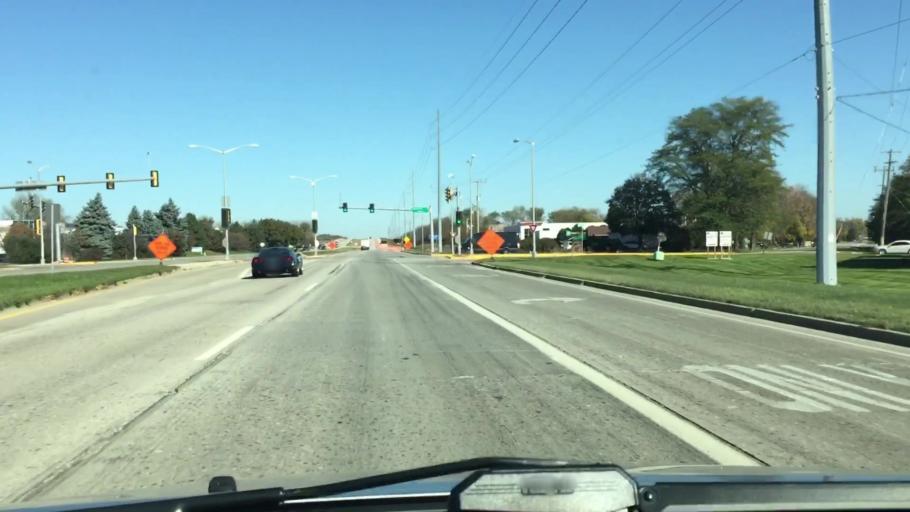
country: US
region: Wisconsin
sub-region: Waukesha County
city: Pewaukee
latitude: 43.0647
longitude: -88.2056
